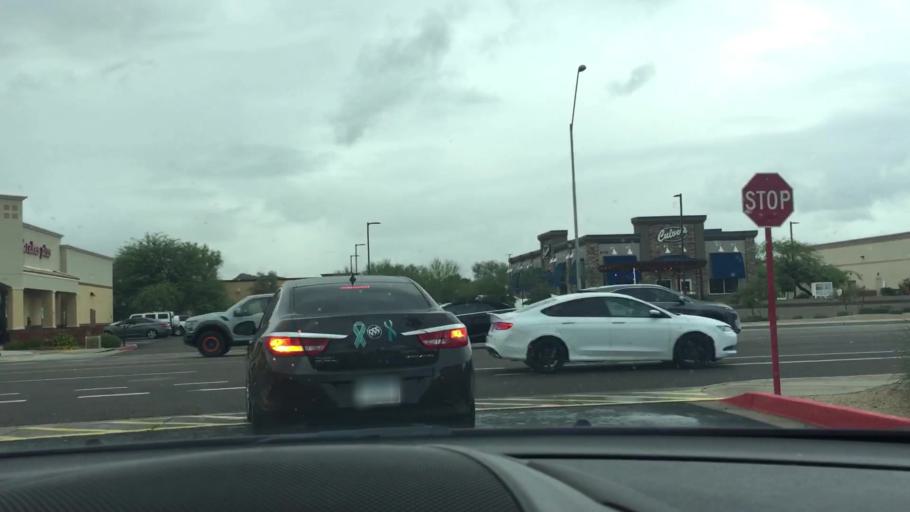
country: US
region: Arizona
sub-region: Maricopa County
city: Sun City
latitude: 33.6814
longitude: -112.2394
